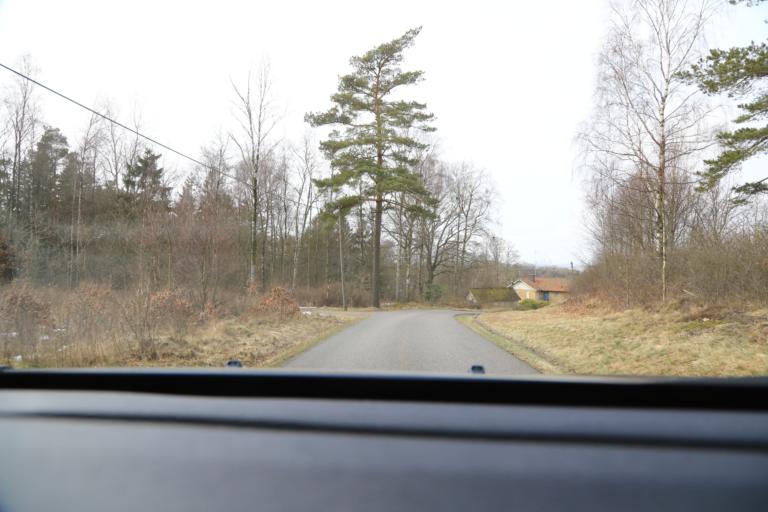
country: SE
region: Halland
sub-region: Varbergs Kommun
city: Veddige
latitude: 57.2154
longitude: 12.2426
